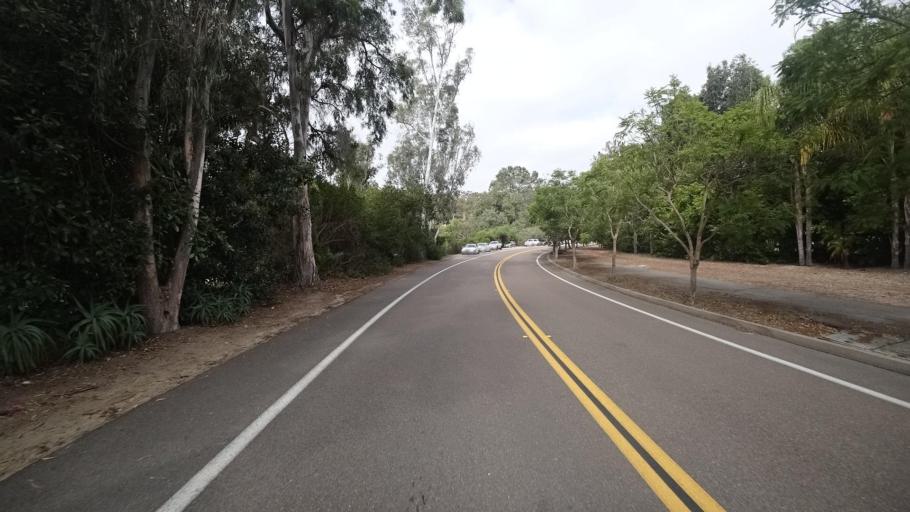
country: US
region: California
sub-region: San Diego County
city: Rancho Santa Fe
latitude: 33.0019
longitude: -117.2331
